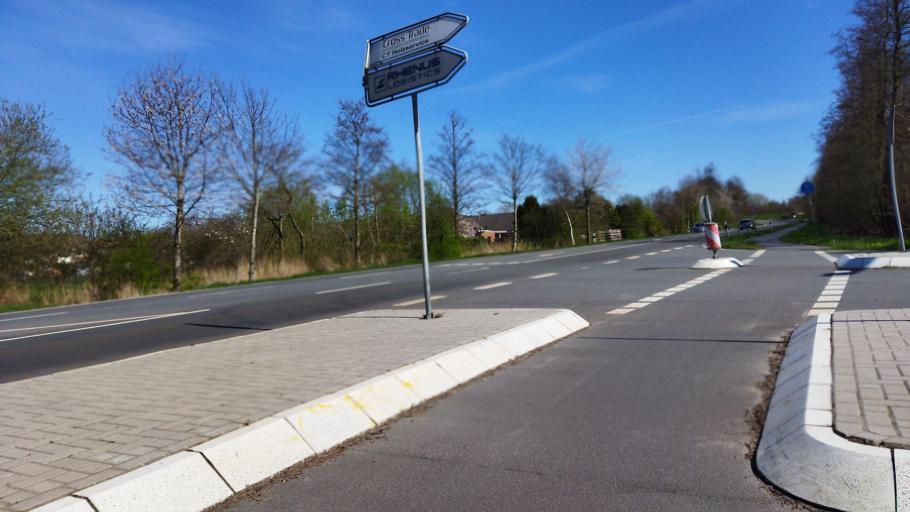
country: DE
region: Bremen
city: Bremerhaven
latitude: 53.5230
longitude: 8.5340
